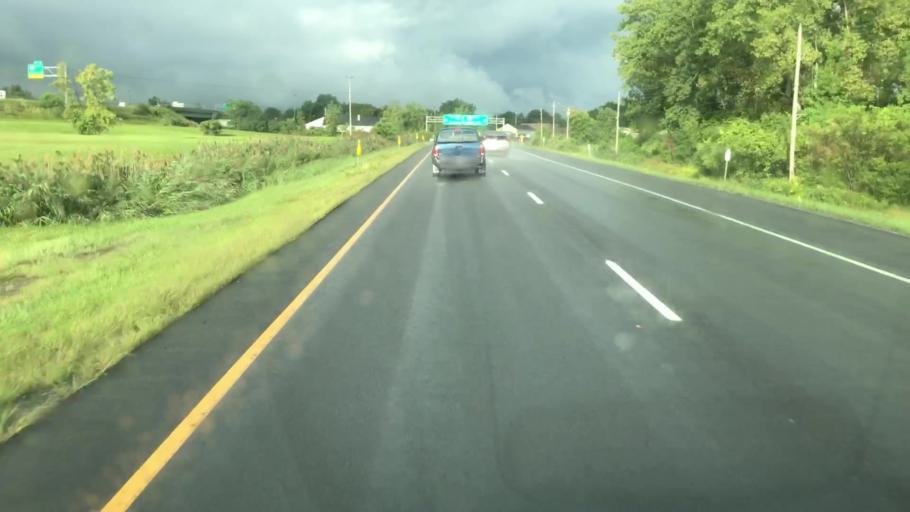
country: US
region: New York
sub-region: Onondaga County
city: Seneca Knolls
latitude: 43.1145
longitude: -76.2668
